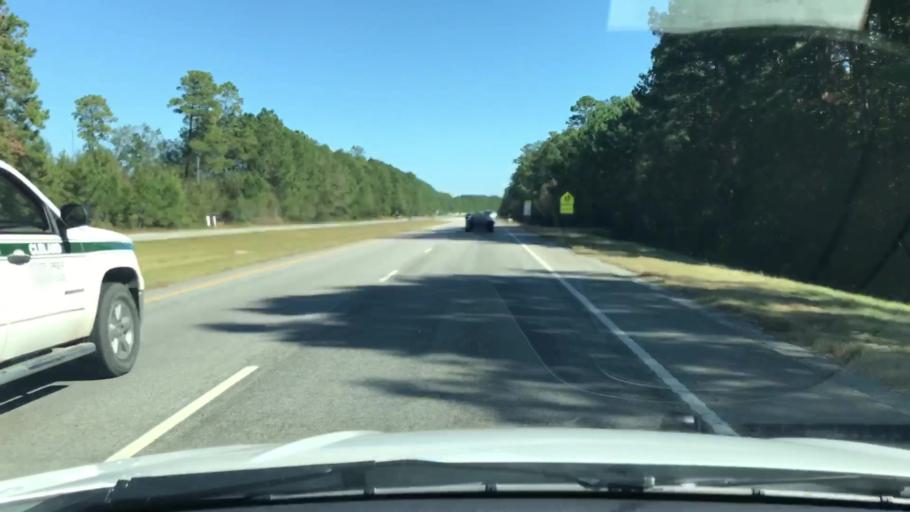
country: US
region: South Carolina
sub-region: Beaufort County
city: Bluffton
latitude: 32.3523
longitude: -80.9187
